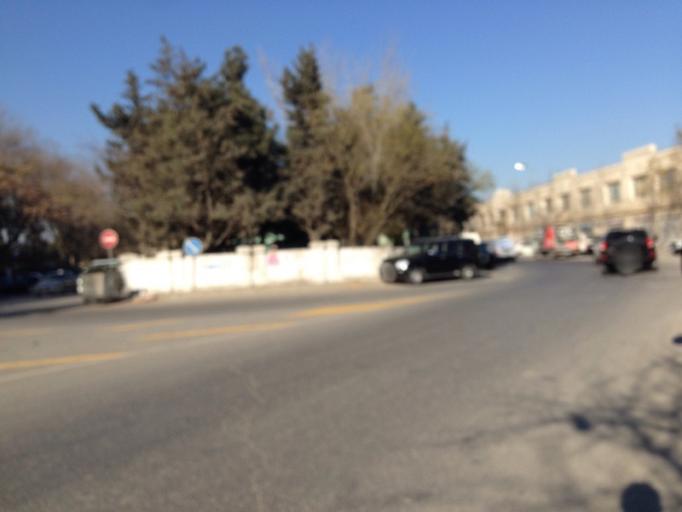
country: AZ
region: Baki
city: Baku
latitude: 40.4110
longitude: 49.8720
